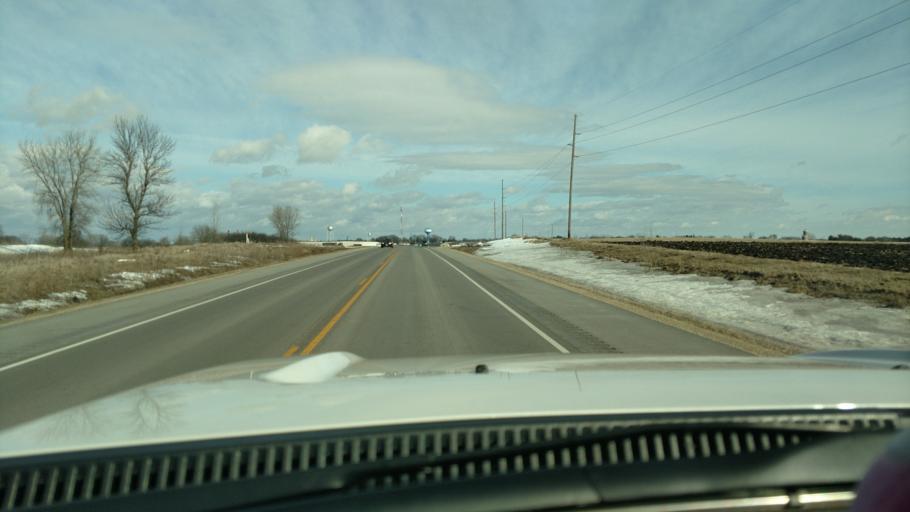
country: US
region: Minnesota
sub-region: Wabasha County
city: Plainview
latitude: 44.1564
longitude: -92.1946
